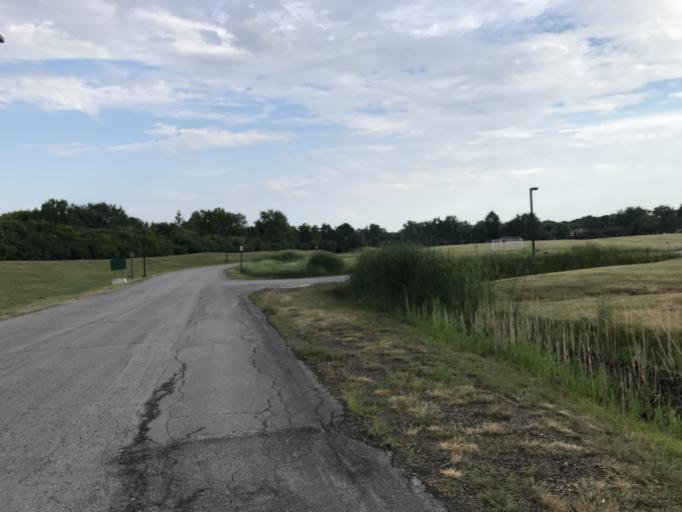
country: US
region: Michigan
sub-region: Oakland County
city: Franklin
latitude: 42.4883
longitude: -83.3298
